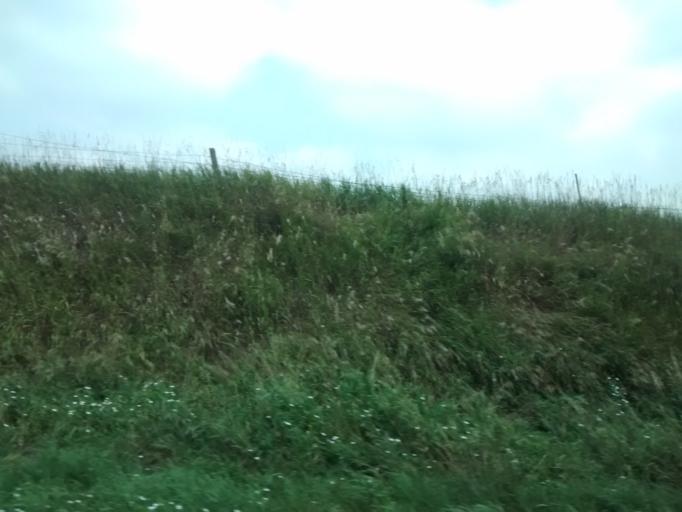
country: US
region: Iowa
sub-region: Woodbury County
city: Moville
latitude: 42.3352
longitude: -96.0458
